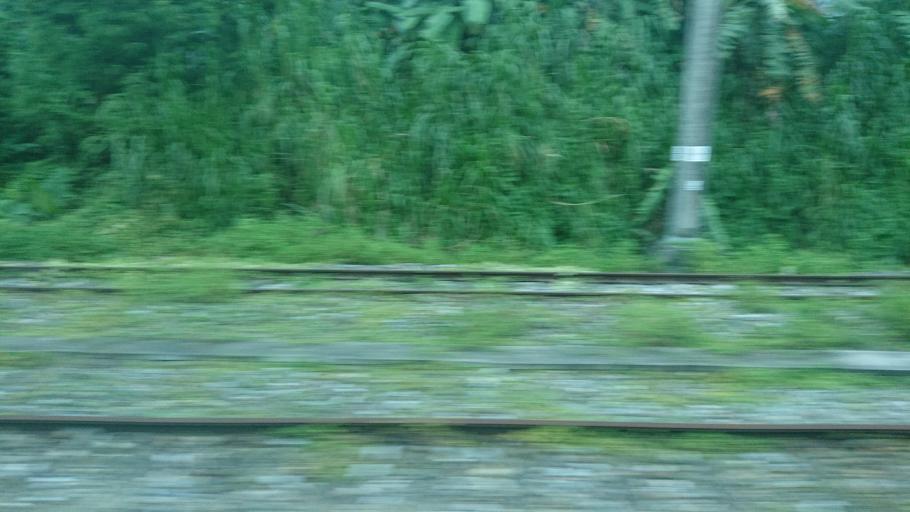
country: TW
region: Taiwan
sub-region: Hualien
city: Hualian
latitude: 24.1229
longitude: 121.6376
